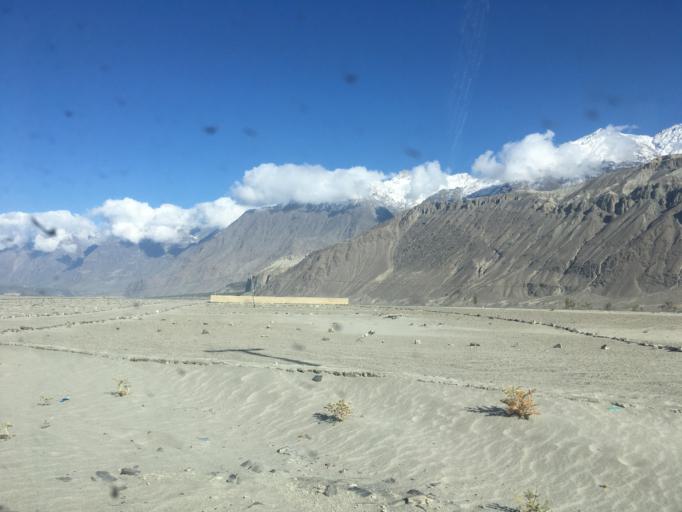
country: PK
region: Gilgit-Baltistan
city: Skardu
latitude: 35.3576
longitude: 75.5429
